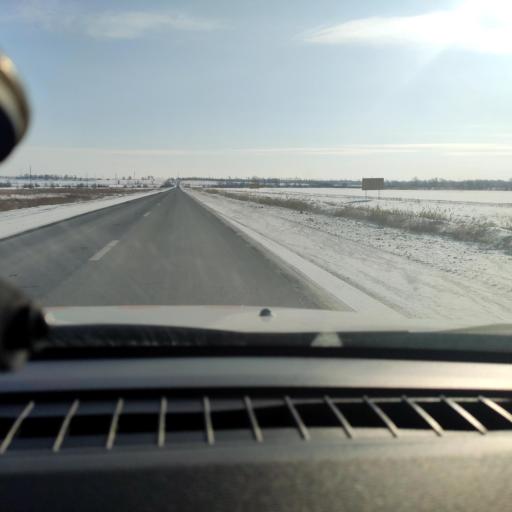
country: RU
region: Samara
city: Smyshlyayevka
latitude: 53.1652
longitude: 50.4570
